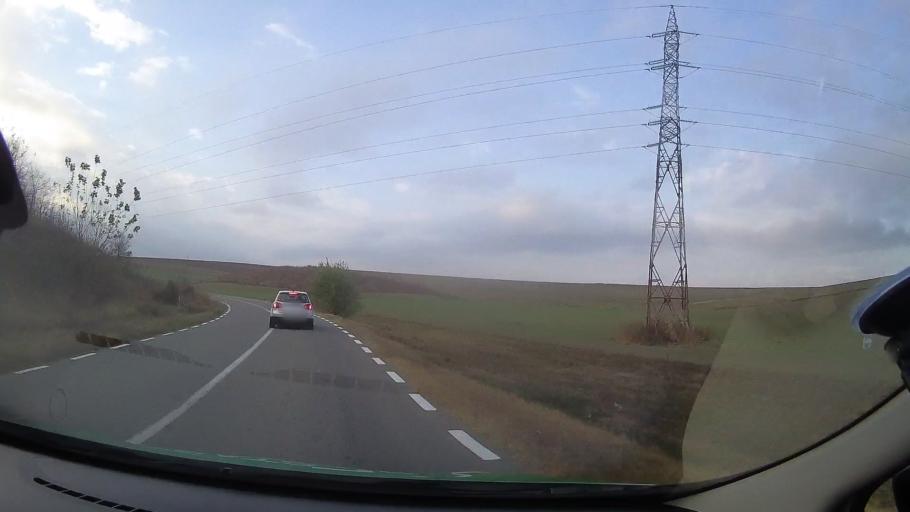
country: RO
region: Constanta
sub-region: Comuna Pestera
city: Pestera
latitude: 44.2032
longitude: 28.1511
